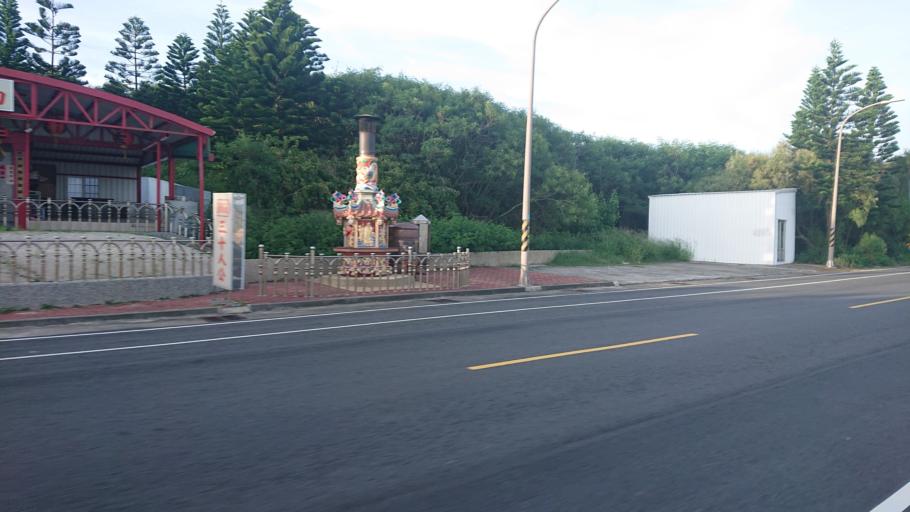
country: TW
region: Taiwan
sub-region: Penghu
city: Ma-kung
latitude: 23.6627
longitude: 119.5744
